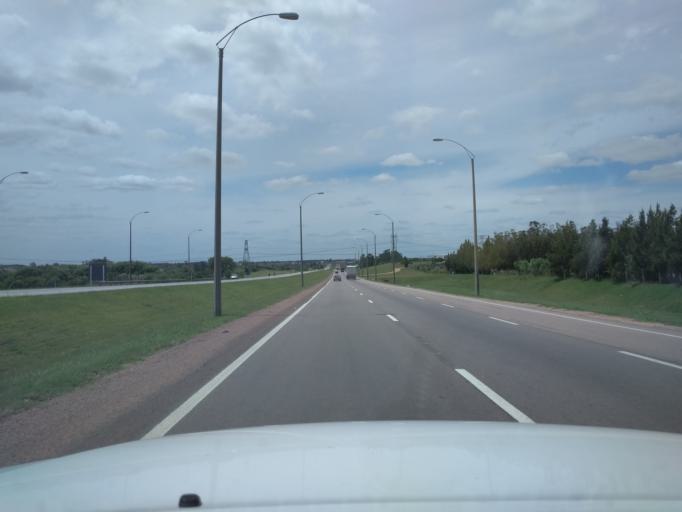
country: UY
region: Canelones
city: La Paz
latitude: -34.7662
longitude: -56.2654
